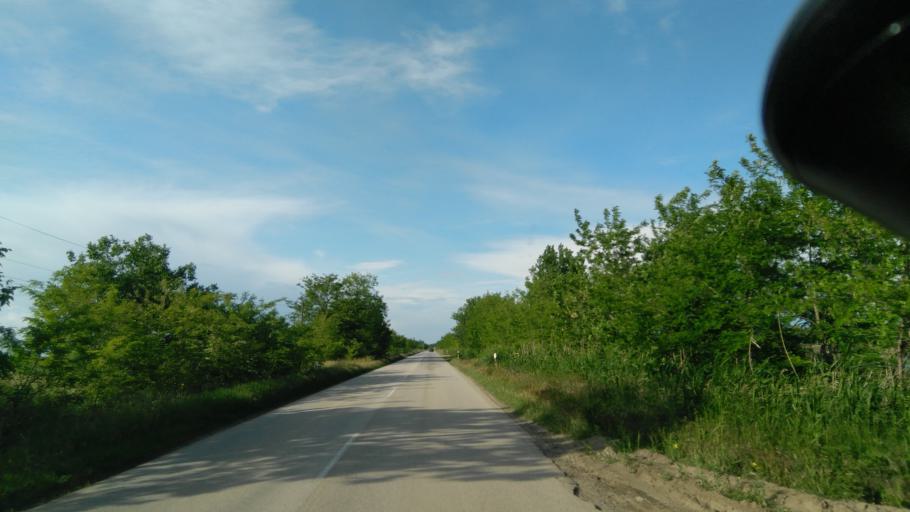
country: HU
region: Bekes
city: Elek
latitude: 46.5726
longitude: 21.2696
